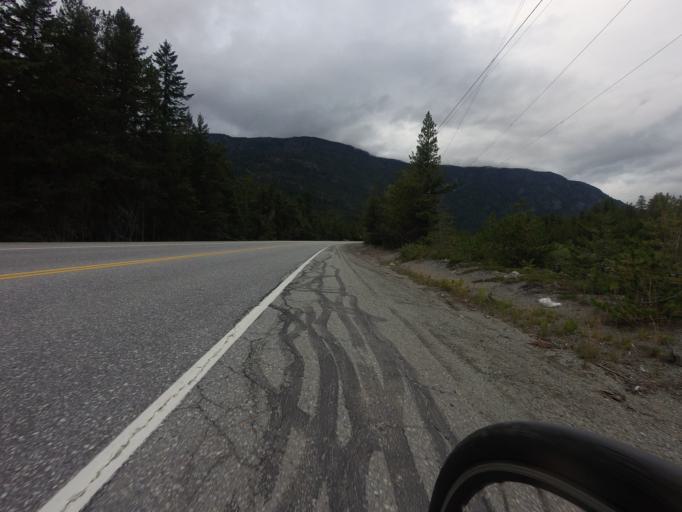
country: CA
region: British Columbia
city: Pemberton
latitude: 50.2656
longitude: -122.8671
